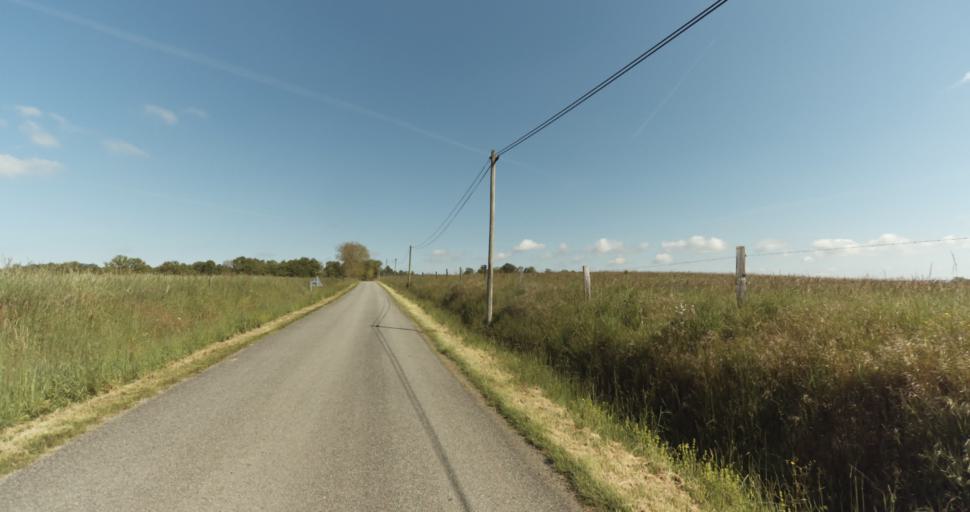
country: FR
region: Limousin
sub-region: Departement de la Haute-Vienne
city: Le Vigen
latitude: 45.7028
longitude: 1.3021
